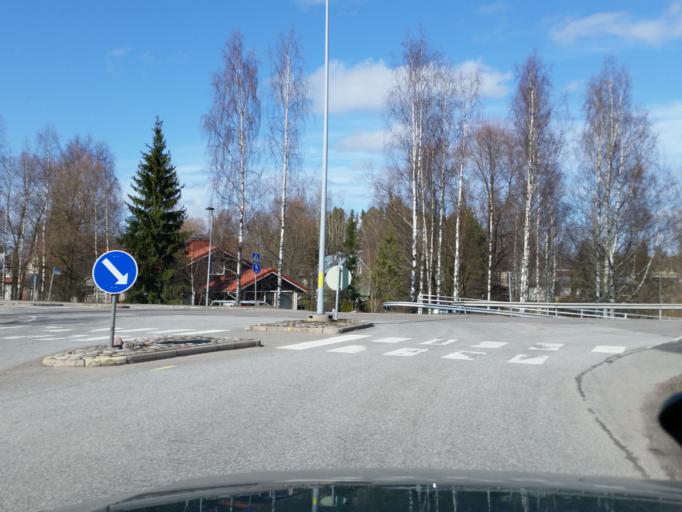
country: FI
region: Uusimaa
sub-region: Helsinki
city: Vihti
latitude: 60.4133
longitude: 24.3303
